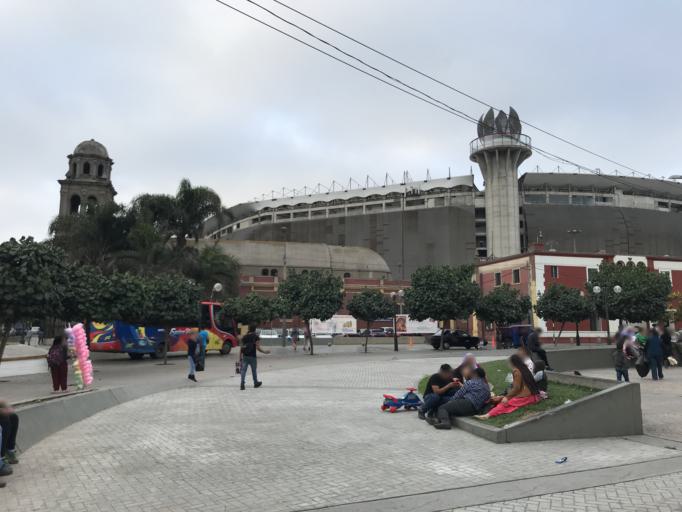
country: PE
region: Lima
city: Lima
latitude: -12.0694
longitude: -77.0342
